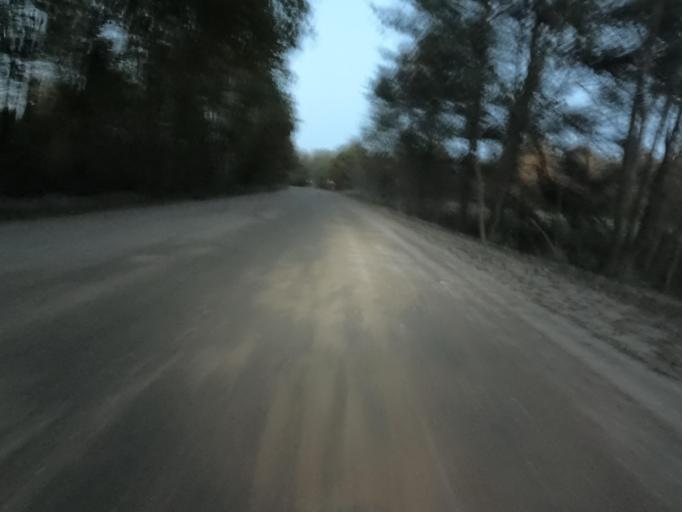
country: RU
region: Leningrad
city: Lyuban'
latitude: 59.1868
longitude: 31.2477
